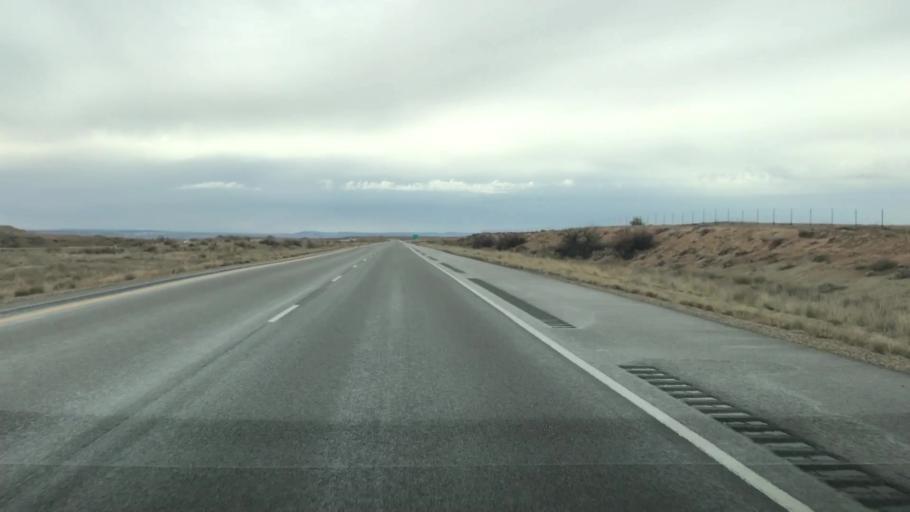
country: US
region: Colorado
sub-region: Mesa County
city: Loma
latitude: 39.0466
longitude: -109.2721
